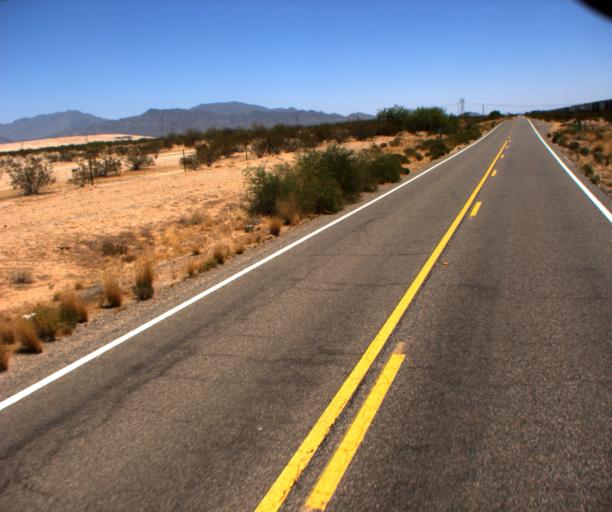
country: US
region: Arizona
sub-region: Pinal County
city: Maricopa
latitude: 33.0477
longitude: -112.3021
